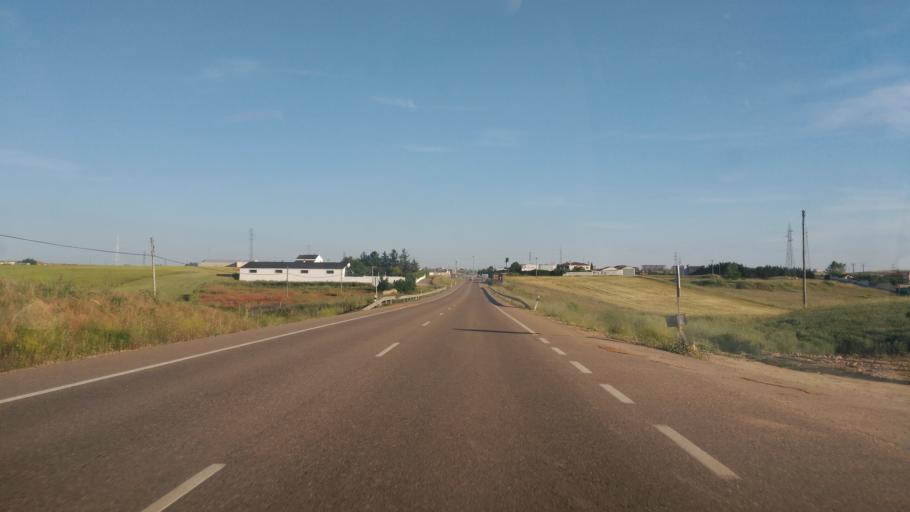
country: ES
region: Castille and Leon
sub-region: Provincia de Salamanca
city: Villares de la Reina
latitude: 41.0081
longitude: -5.6684
